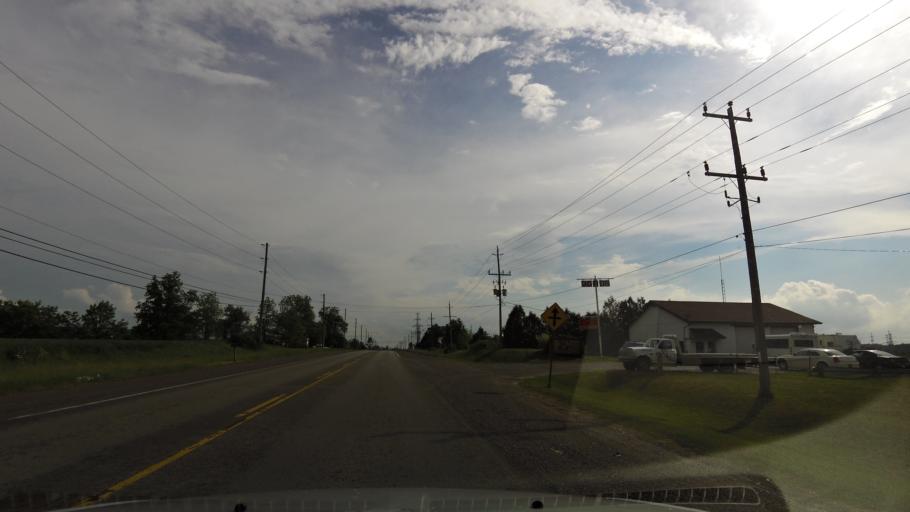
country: CA
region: Ontario
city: Ancaster
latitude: 43.0563
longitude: -79.9668
